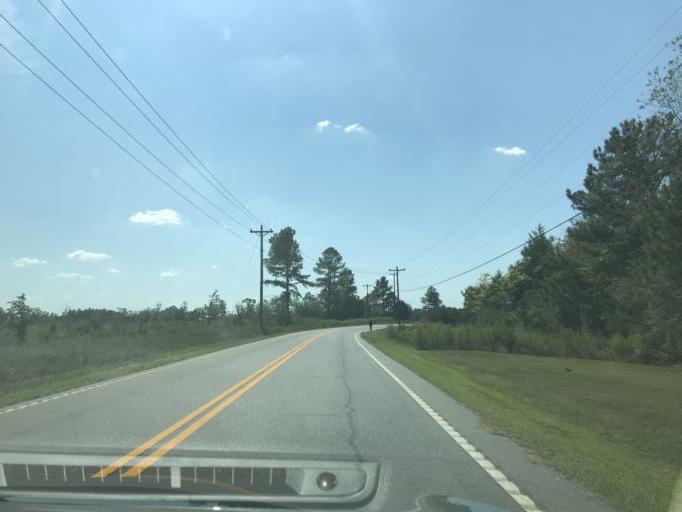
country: US
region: South Carolina
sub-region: Cherokee County
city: Gaffney
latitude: 35.1015
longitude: -81.7068
